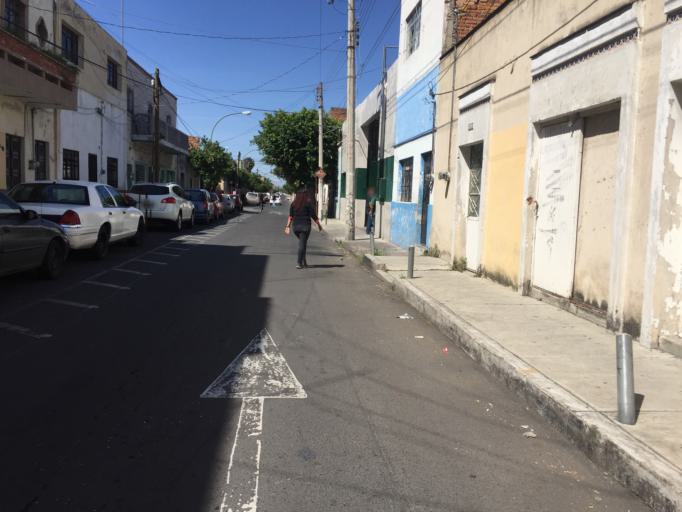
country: MX
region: Jalisco
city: Guadalajara
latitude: 20.6848
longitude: -103.3621
